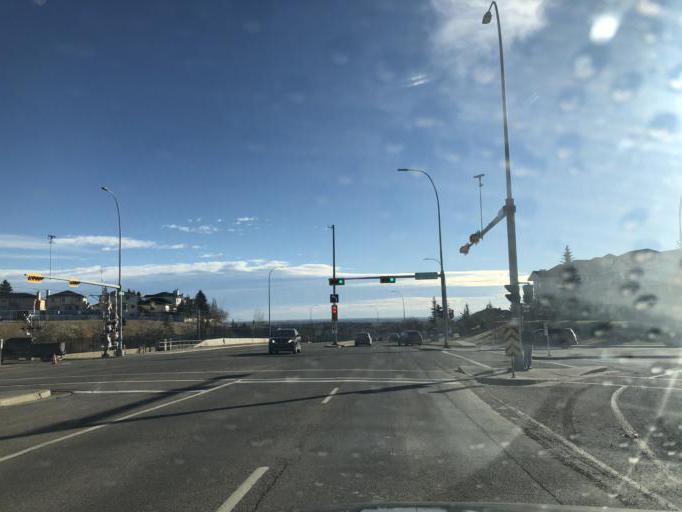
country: CA
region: Alberta
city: Calgary
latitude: 51.0370
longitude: -114.1794
